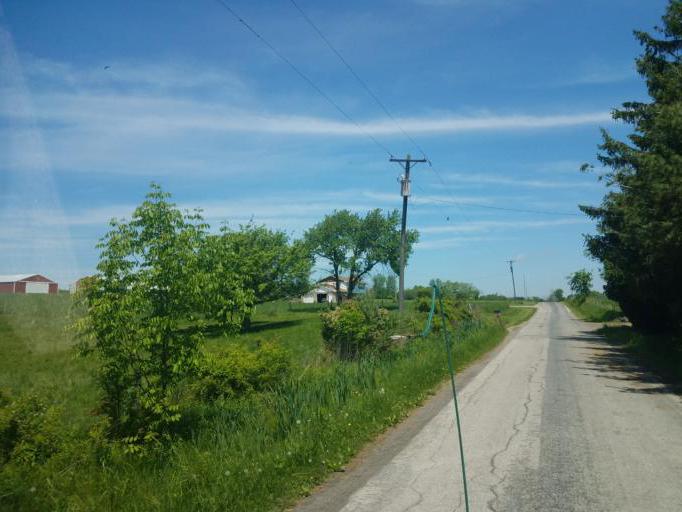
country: US
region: Ohio
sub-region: Wayne County
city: West Salem
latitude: 40.9470
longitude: -82.1788
